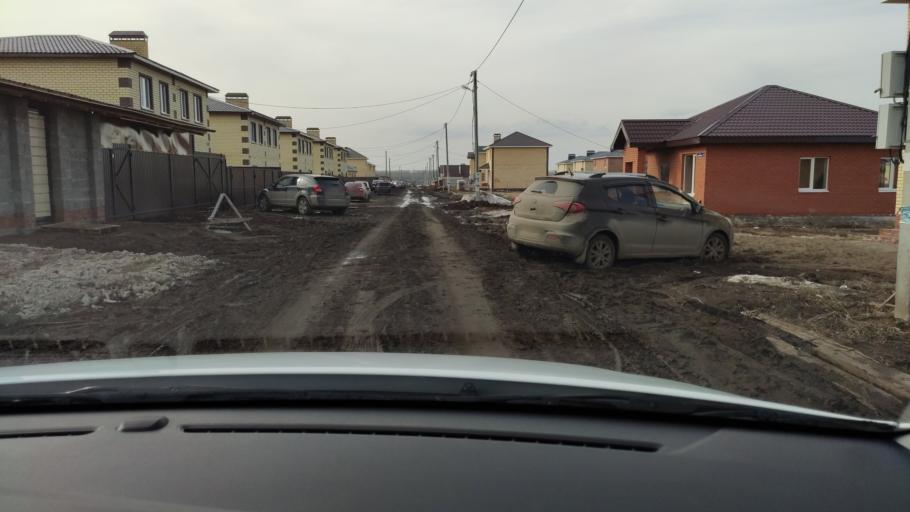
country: RU
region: Tatarstan
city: Stolbishchi
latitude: 55.7185
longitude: 49.3304
